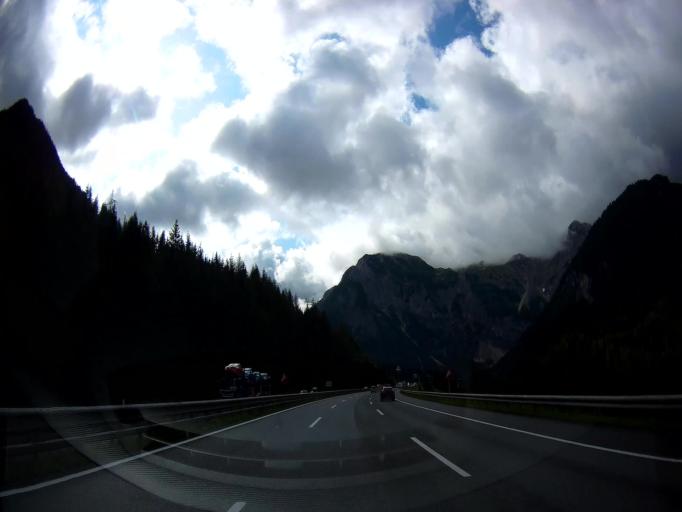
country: AT
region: Salzburg
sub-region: Politischer Bezirk Sankt Johann im Pongau
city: Flachau
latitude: 47.2572
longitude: 13.4188
